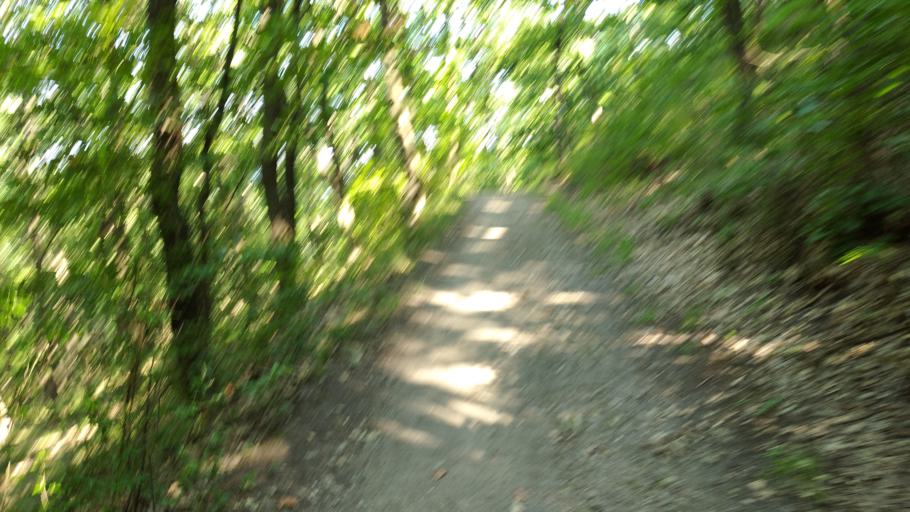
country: HU
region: Nograd
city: Nagyoroszi
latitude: 48.0169
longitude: 19.0343
